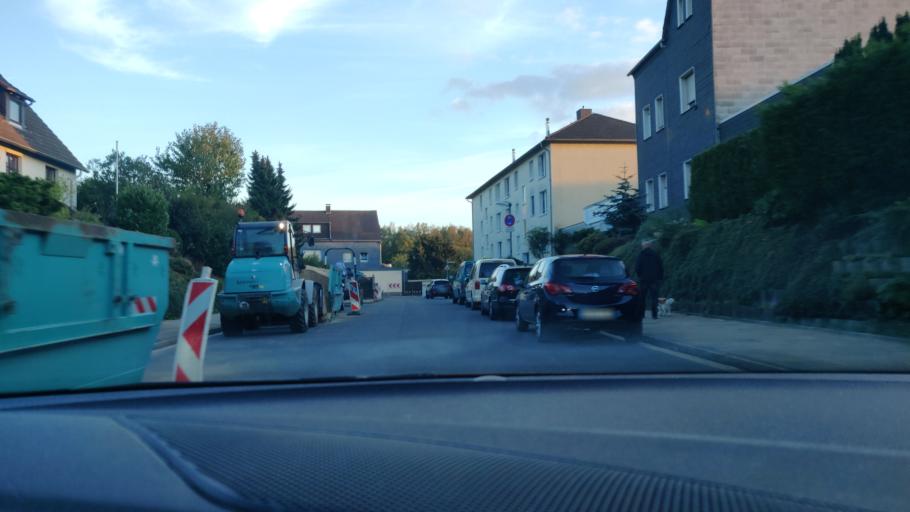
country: DE
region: North Rhine-Westphalia
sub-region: Regierungsbezirk Dusseldorf
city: Velbert
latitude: 51.3136
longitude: 7.0614
